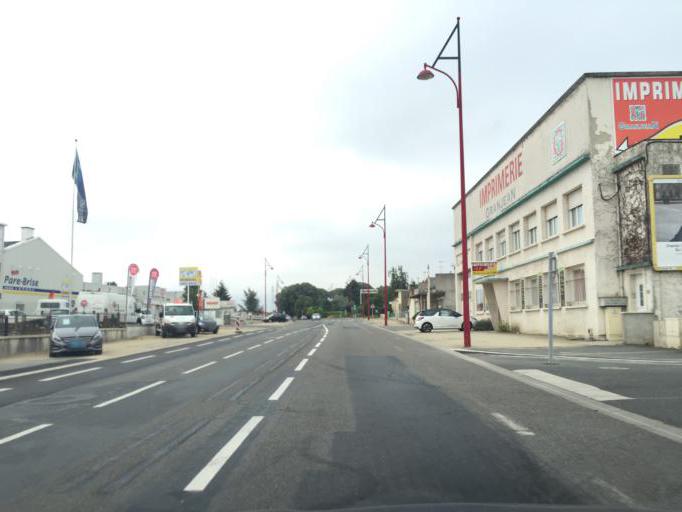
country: FR
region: Auvergne
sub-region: Departement de l'Allier
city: Avermes
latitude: 46.5827
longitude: 3.3193
